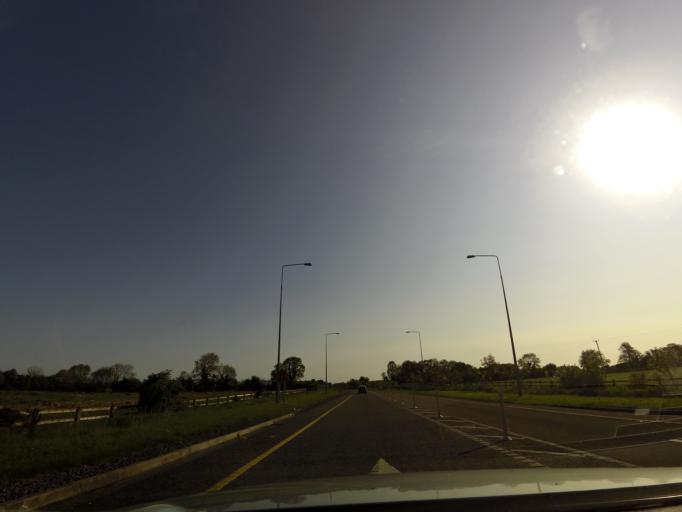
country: IE
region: Munster
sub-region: North Tipperary
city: Nenagh
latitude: 52.8481
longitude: -8.1560
